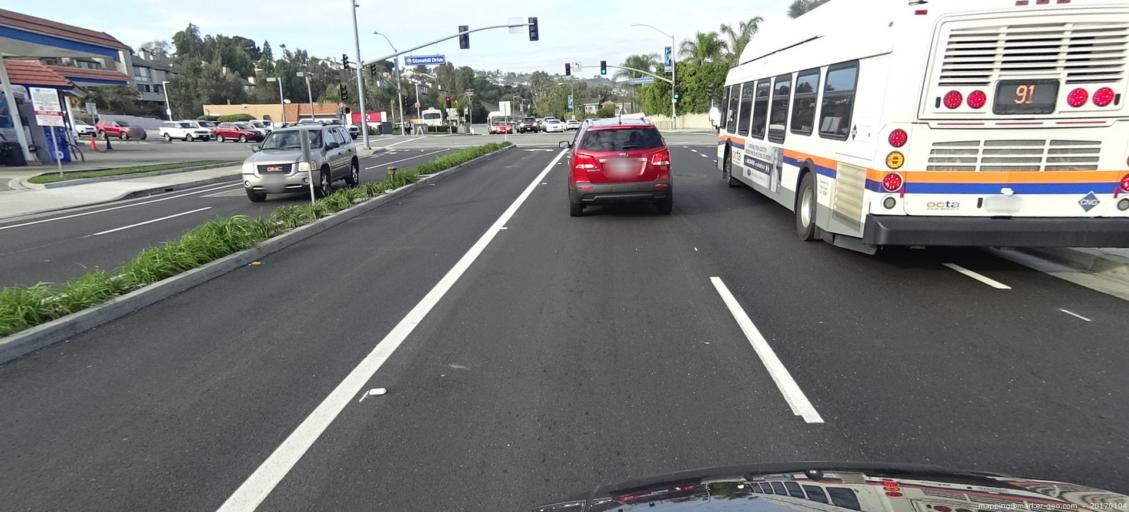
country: US
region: California
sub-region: Orange County
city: Dana Point
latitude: 33.4749
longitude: -117.6849
